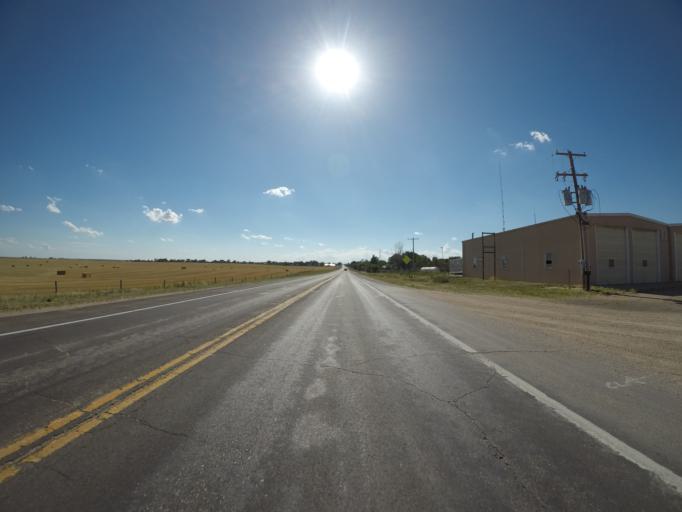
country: US
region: Colorado
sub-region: Logan County
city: Sterling
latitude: 40.6238
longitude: -103.2874
